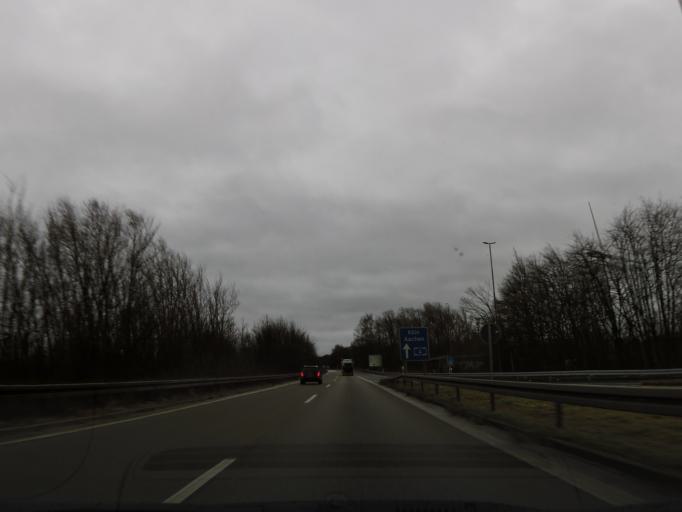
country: NL
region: Limburg
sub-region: Gemeente Vaals
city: Vaals
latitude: 50.8170
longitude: 6.0262
